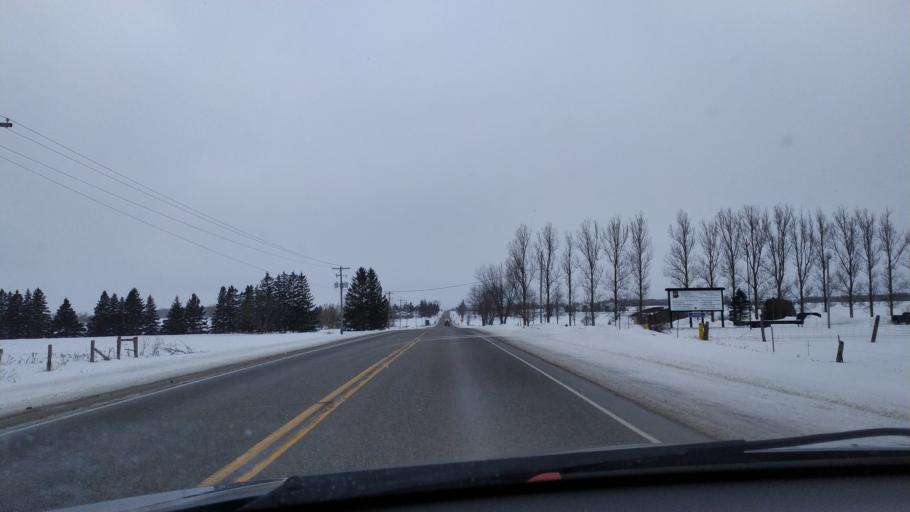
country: CA
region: Ontario
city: North Perth
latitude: 43.5949
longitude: -80.8905
